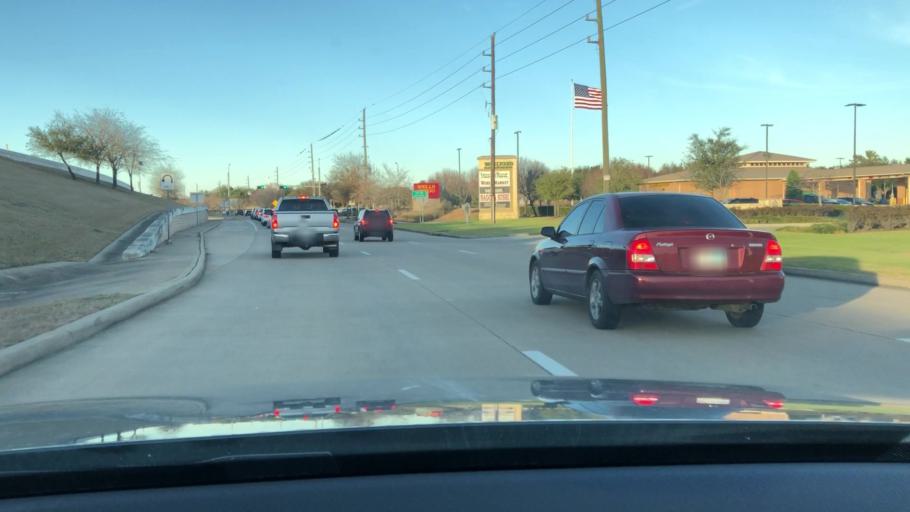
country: US
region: Texas
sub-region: Fort Bend County
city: Cinco Ranch
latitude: 29.7127
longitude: -95.7734
